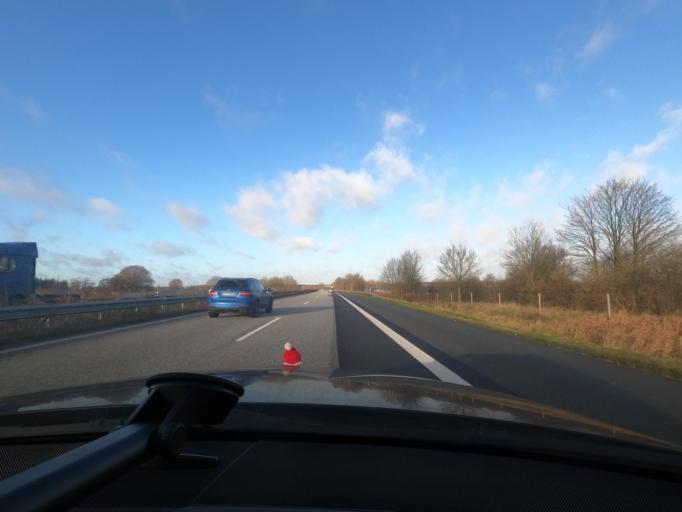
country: DE
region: Schleswig-Holstein
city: Lurschau
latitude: 54.5818
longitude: 9.4670
